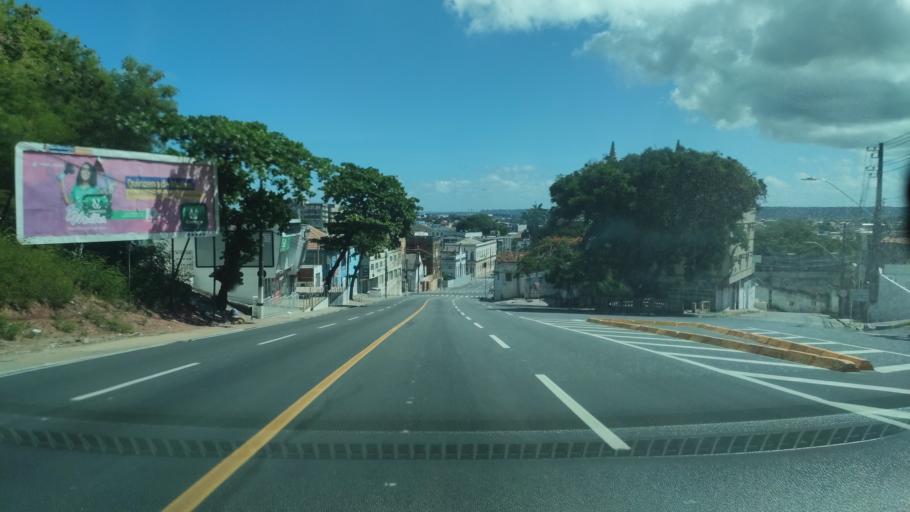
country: BR
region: Alagoas
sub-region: Maceio
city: Maceio
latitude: -9.6596
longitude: -35.7374
